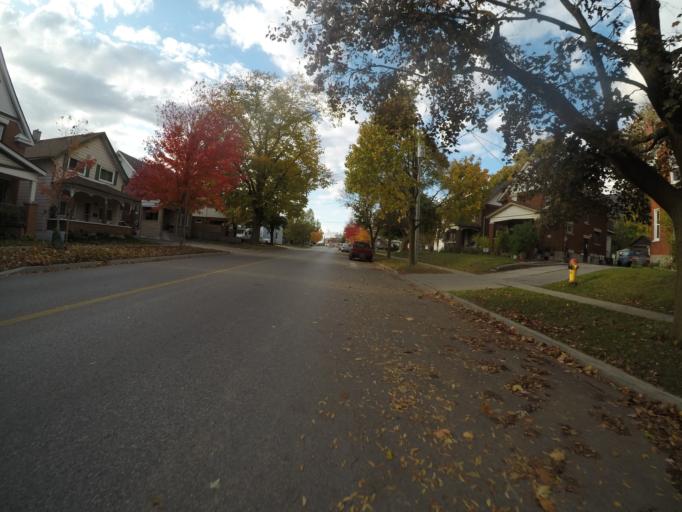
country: CA
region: Ontario
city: Waterloo
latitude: 43.4533
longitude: -80.5091
